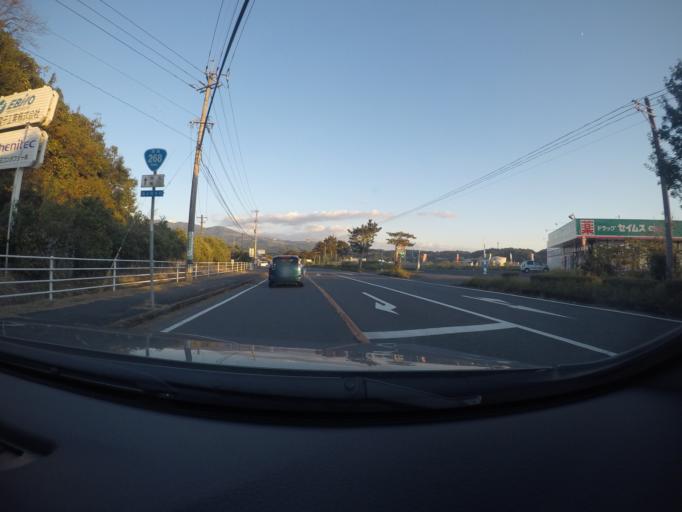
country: JP
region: Kagoshima
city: Okuchi-shinohara
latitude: 31.9540
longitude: 130.7124
